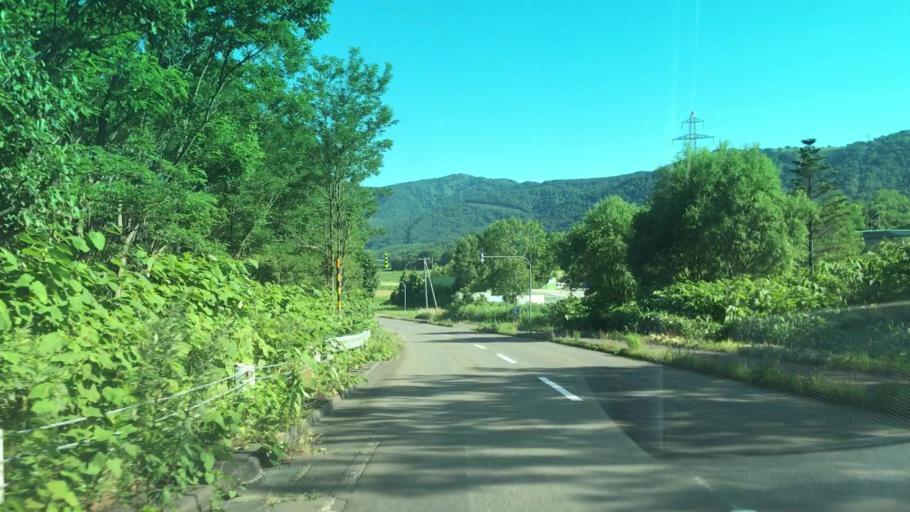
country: JP
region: Hokkaido
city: Yoichi
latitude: 43.0600
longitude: 140.7133
